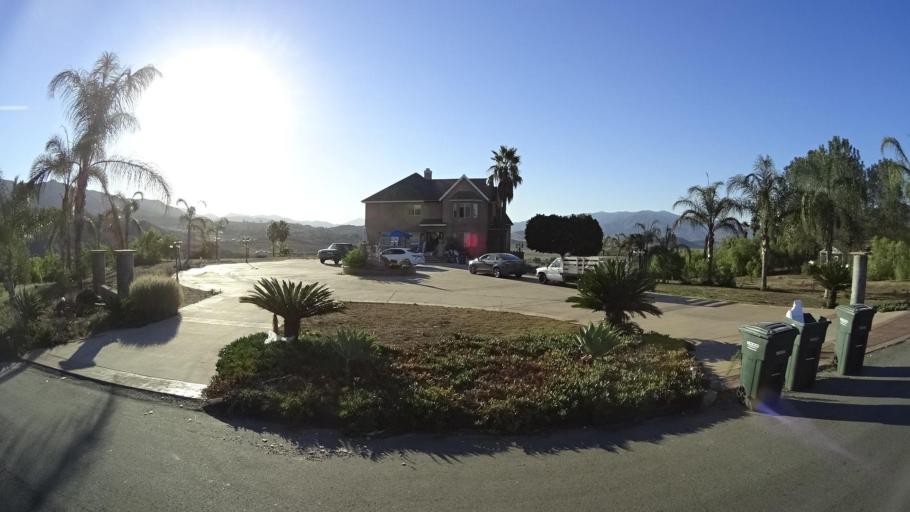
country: US
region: California
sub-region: San Diego County
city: Jamul
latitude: 32.7124
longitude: -116.8652
